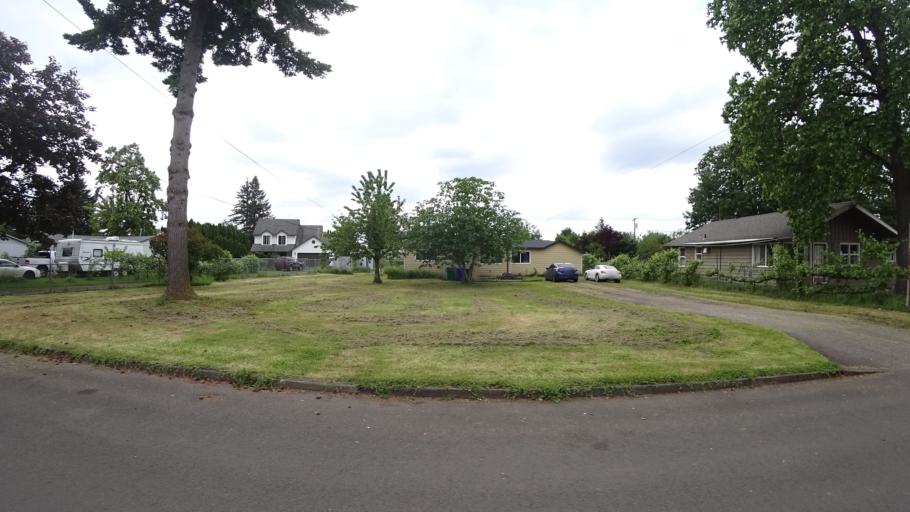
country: US
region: Oregon
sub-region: Multnomah County
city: Gresham
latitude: 45.5069
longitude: -122.4880
